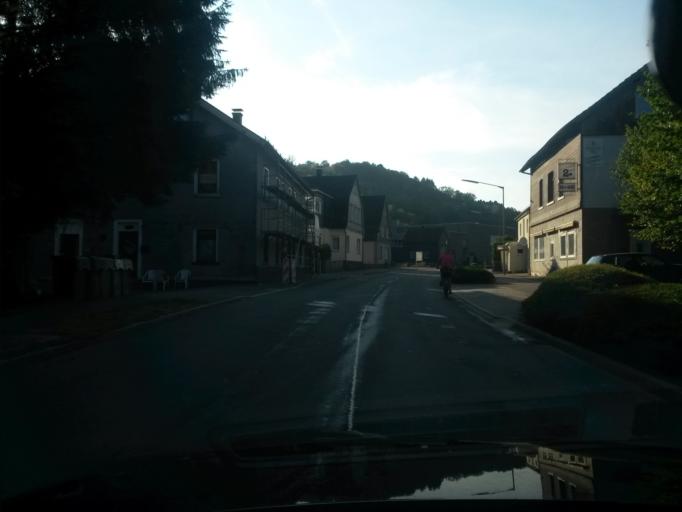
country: DE
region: North Rhine-Westphalia
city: Bergneustadt
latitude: 51.0195
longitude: 7.6176
